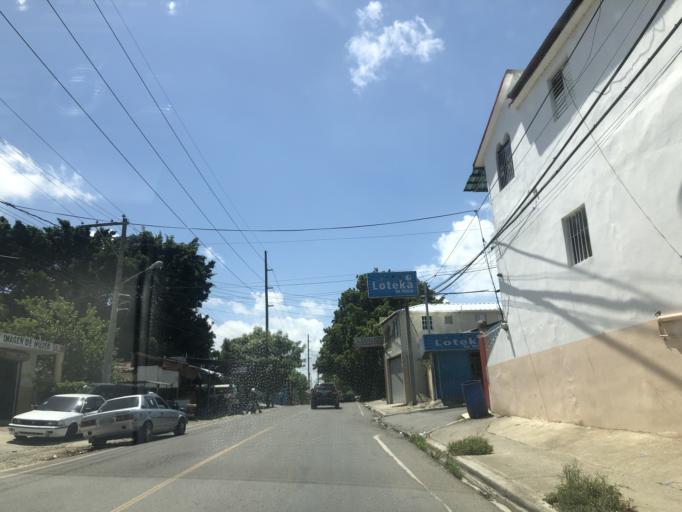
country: DO
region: Santiago
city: La Canela
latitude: 19.4525
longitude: -70.7605
